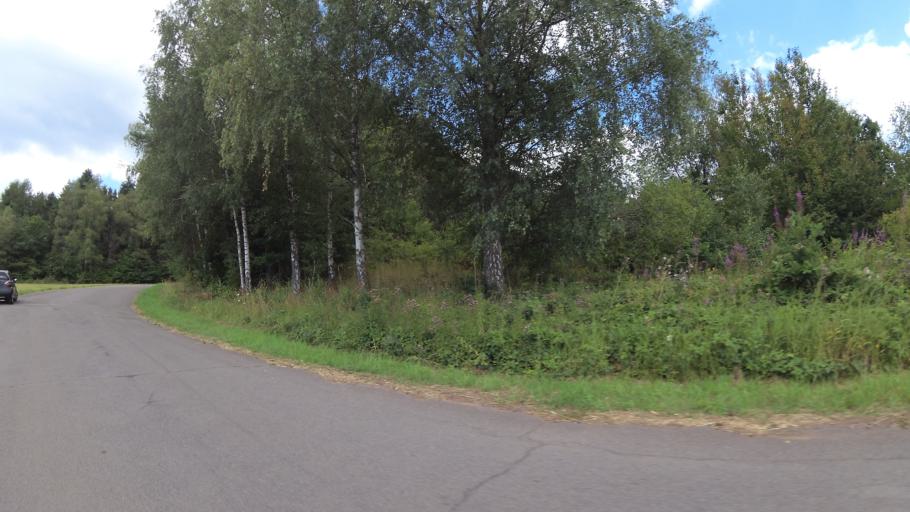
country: DE
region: Saarland
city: Weiskirchen
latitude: 49.5633
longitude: 6.8166
